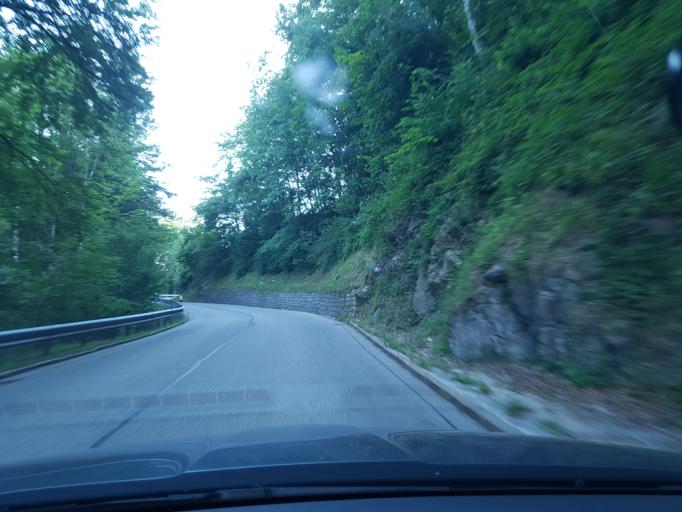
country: DE
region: Bavaria
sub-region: Upper Bavaria
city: Berchtesgaden
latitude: 47.6510
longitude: 13.0025
